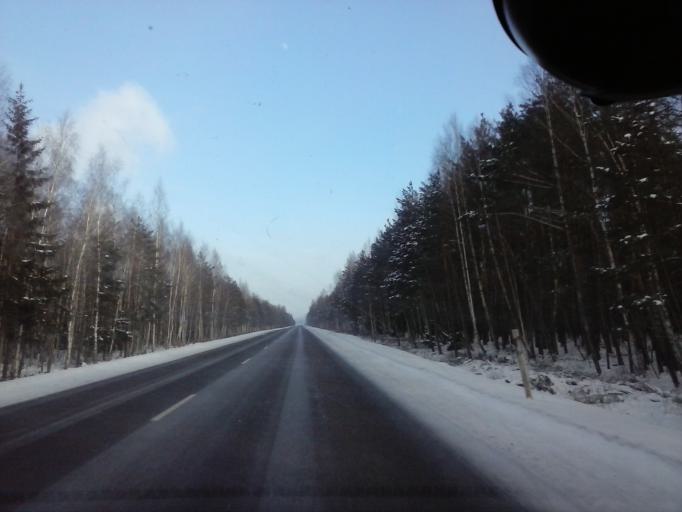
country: EE
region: Tartu
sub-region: Puhja vald
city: Puhja
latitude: 58.3271
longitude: 26.2352
